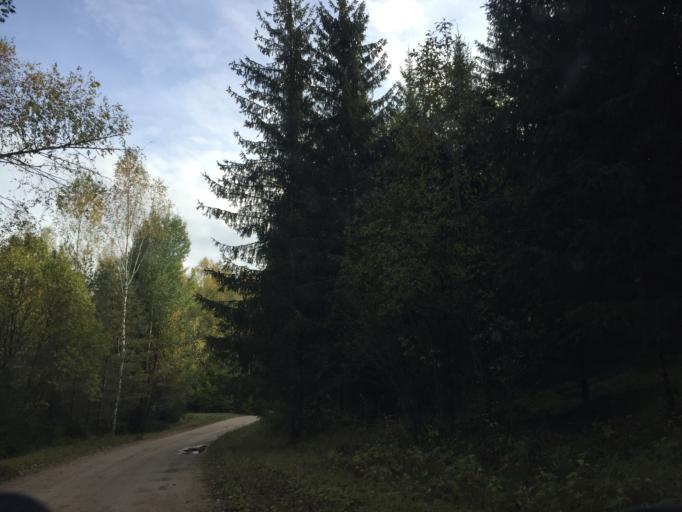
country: LV
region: Jaunpils
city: Jaunpils
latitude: 56.5875
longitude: 23.0108
